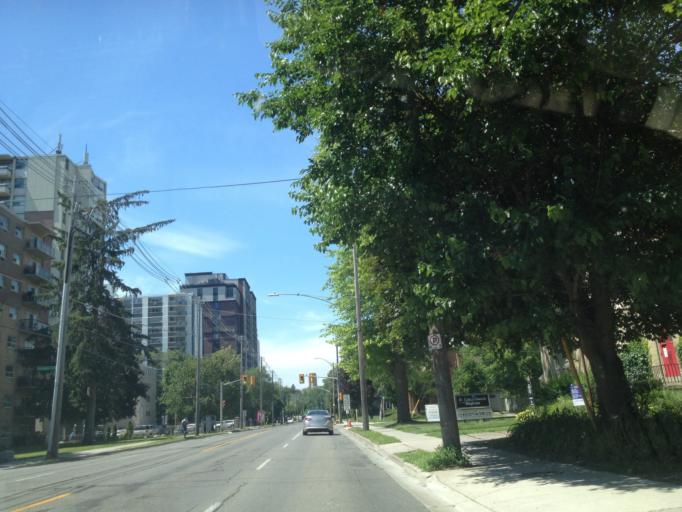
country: CA
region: Ontario
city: London
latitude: 43.0110
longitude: -81.2633
